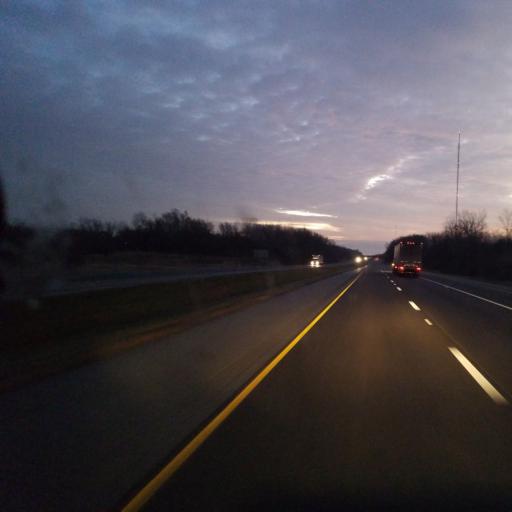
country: US
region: Illinois
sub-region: Tazewell County
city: Creve Coeur
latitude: 40.6301
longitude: -89.5793
